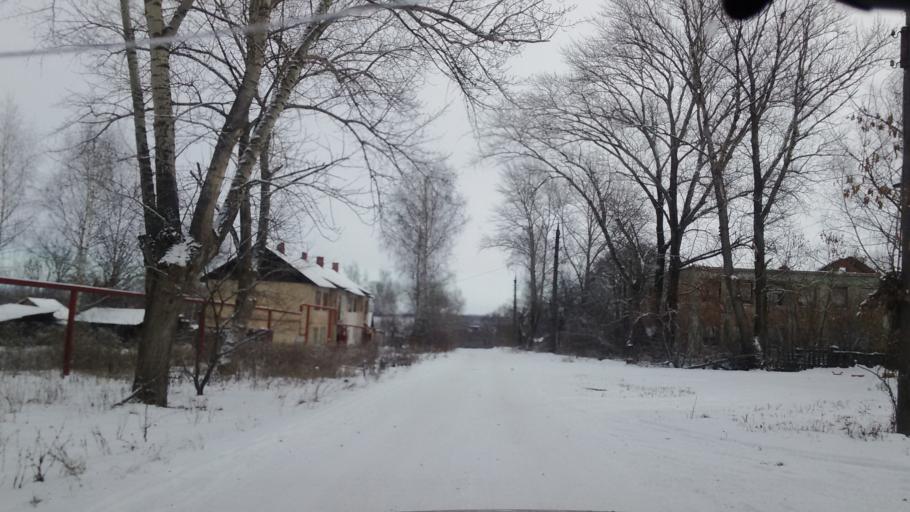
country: RU
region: Tula
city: Bogoroditsk
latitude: 53.7585
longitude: 38.1172
